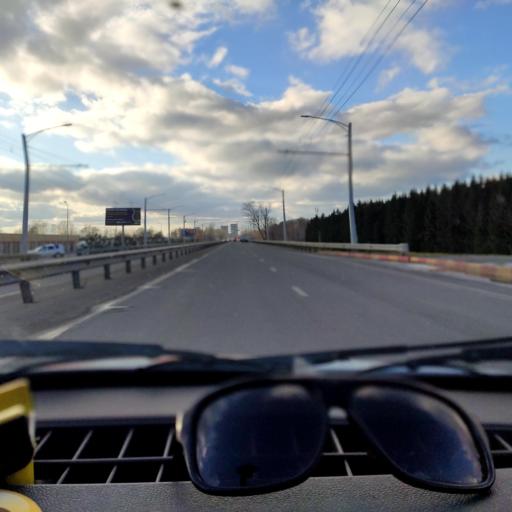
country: RU
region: Bashkortostan
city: Ufa
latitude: 54.7659
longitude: 55.9413
